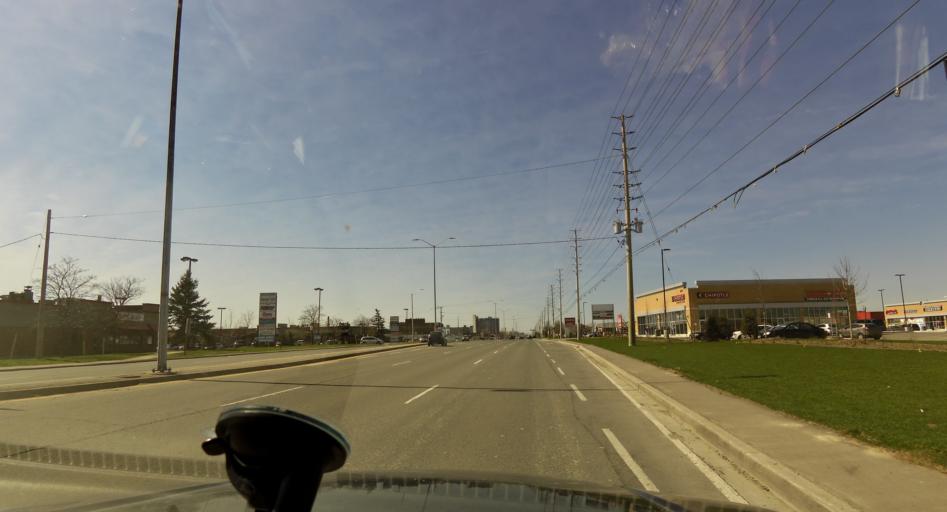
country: CA
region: Ontario
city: Etobicoke
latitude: 43.6368
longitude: -79.6219
